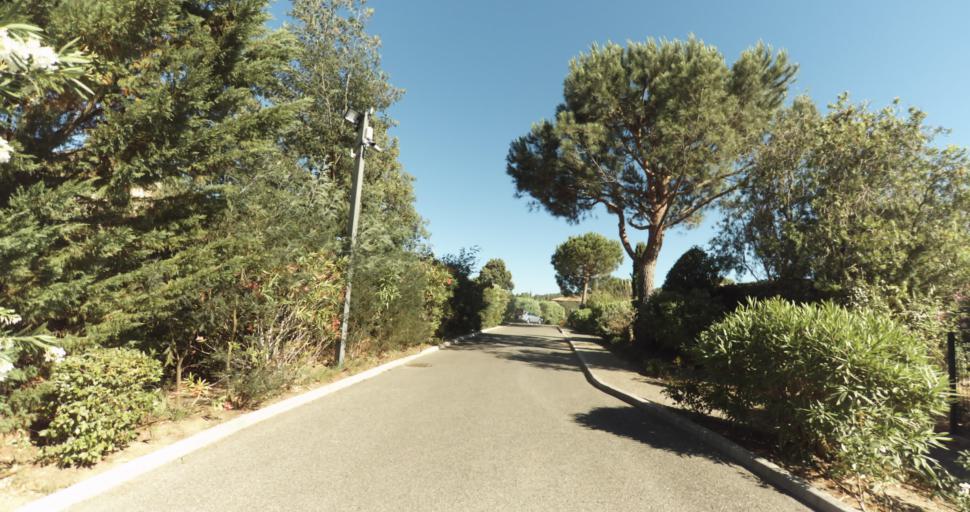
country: FR
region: Provence-Alpes-Cote d'Azur
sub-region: Departement du Var
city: Gassin
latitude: 43.2537
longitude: 6.6061
